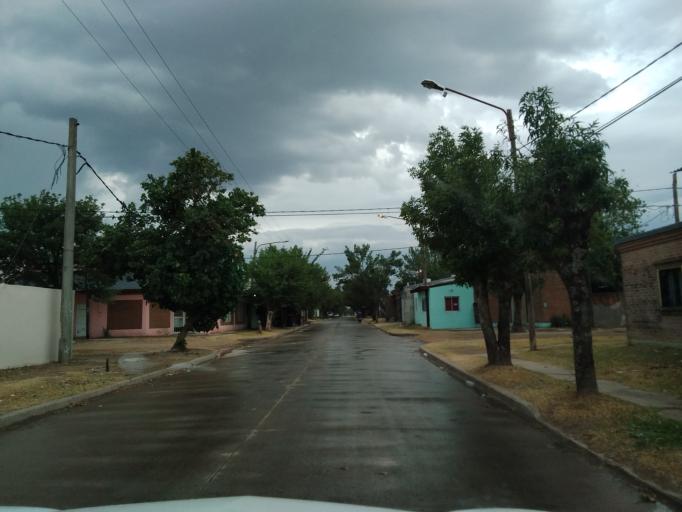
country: AR
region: Corrientes
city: Corrientes
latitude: -27.5196
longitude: -58.7891
